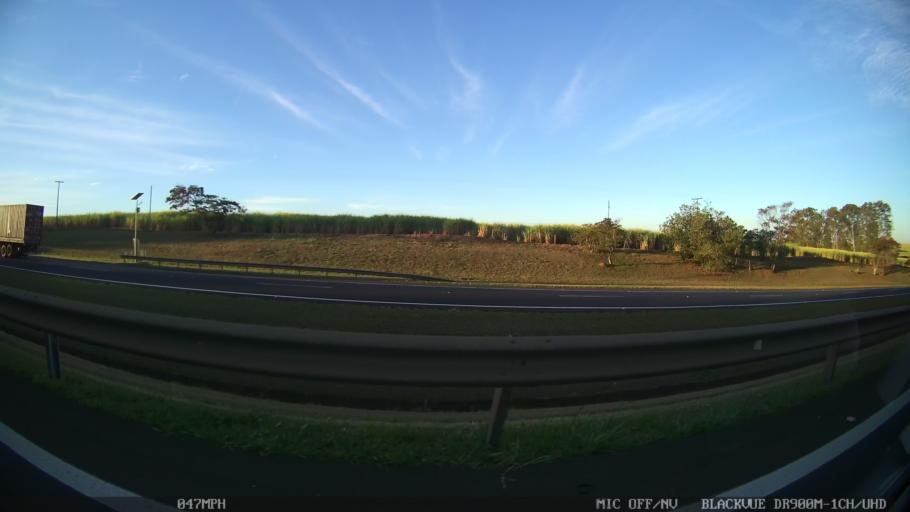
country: BR
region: Sao Paulo
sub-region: Catanduva
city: Catanduva
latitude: -21.0723
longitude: -49.1001
